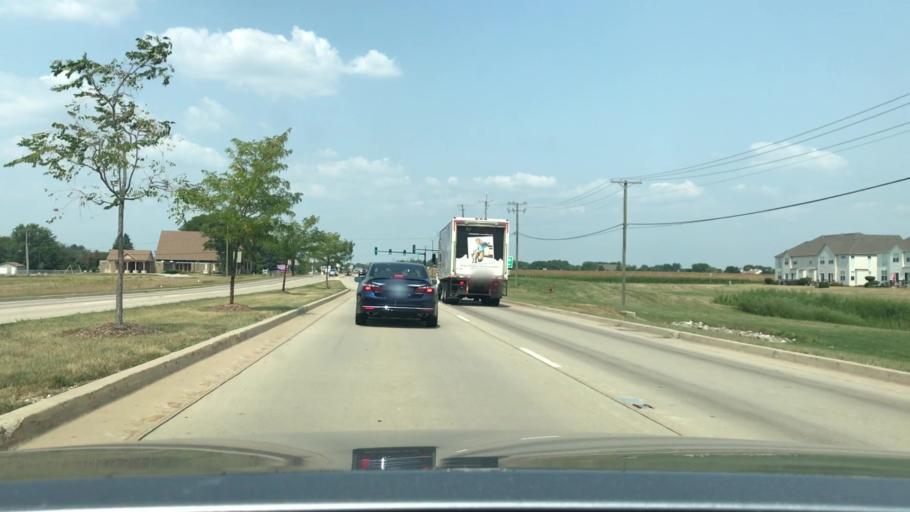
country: US
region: Illinois
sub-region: Will County
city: Plainfield
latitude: 41.5849
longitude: -88.2012
